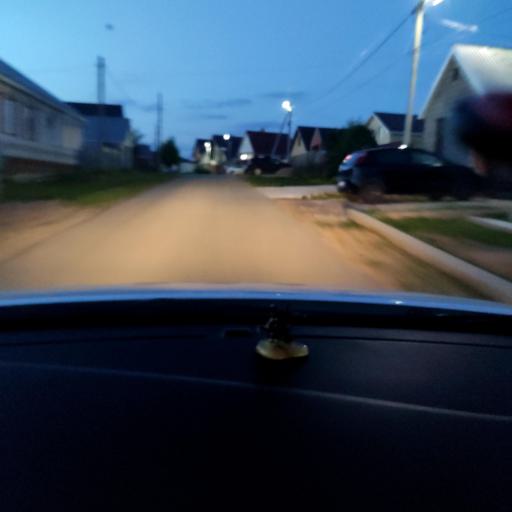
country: RU
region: Tatarstan
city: Vysokaya Gora
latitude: 55.9035
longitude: 49.3161
